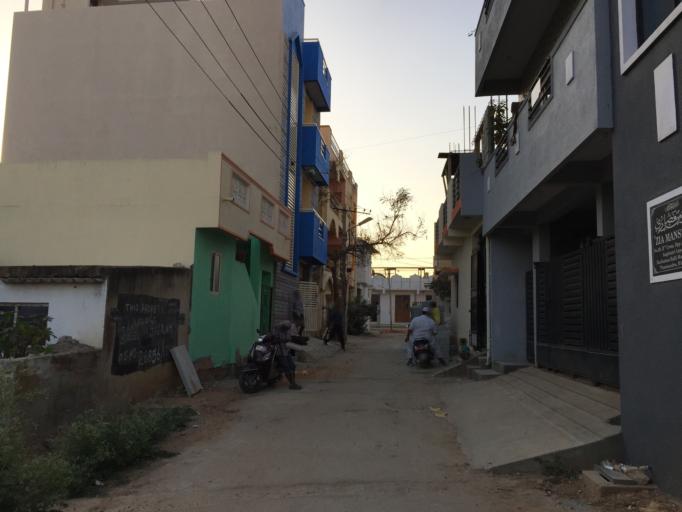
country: IN
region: Karnataka
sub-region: Bangalore Urban
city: Yelahanka
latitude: 13.0554
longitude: 77.6274
